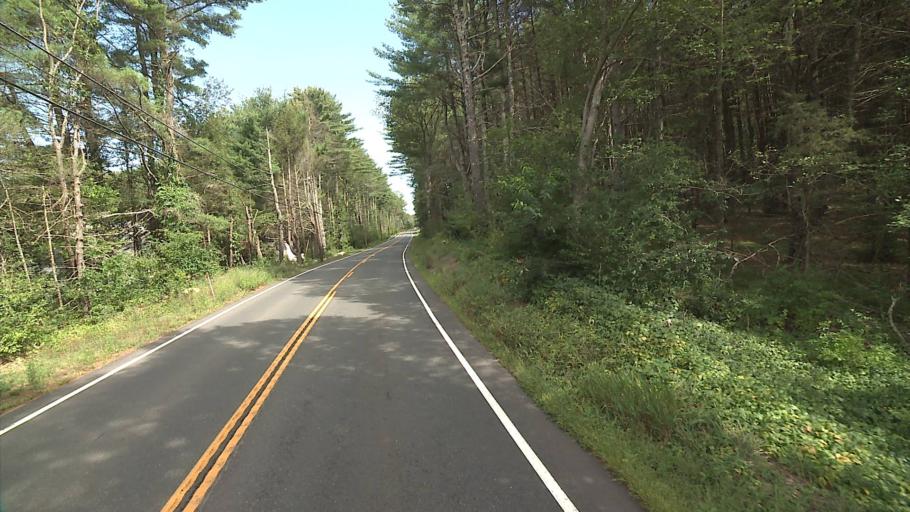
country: US
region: Connecticut
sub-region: Tolland County
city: Stafford
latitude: 42.0055
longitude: -72.3182
